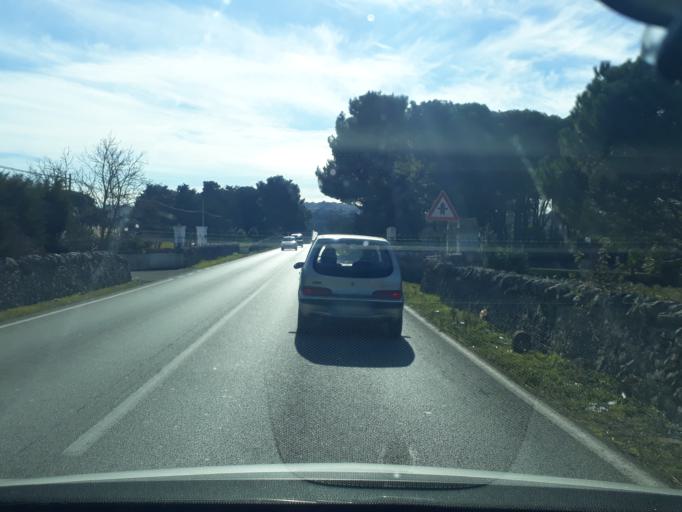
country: IT
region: Apulia
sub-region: Provincia di Taranto
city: Martina Franca
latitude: 40.7239
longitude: 17.3327
